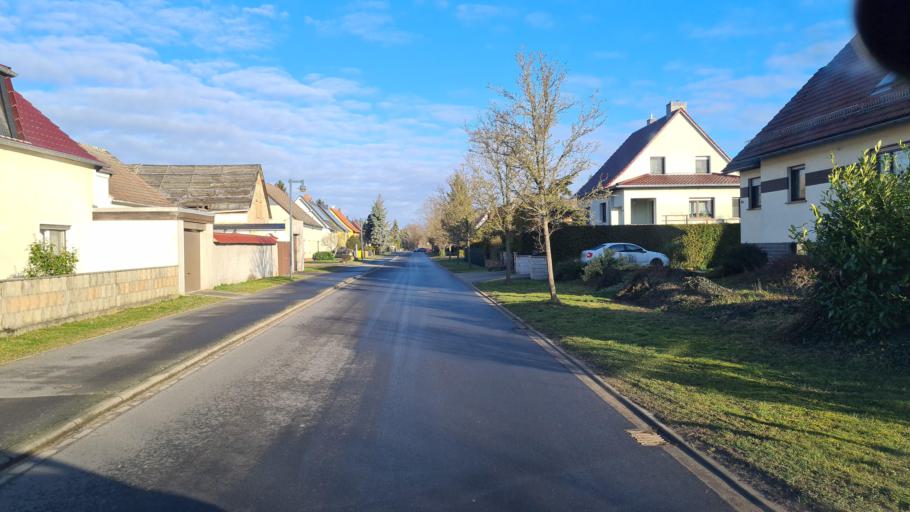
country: DE
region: Brandenburg
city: Herzberg
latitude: 51.6995
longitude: 13.2177
